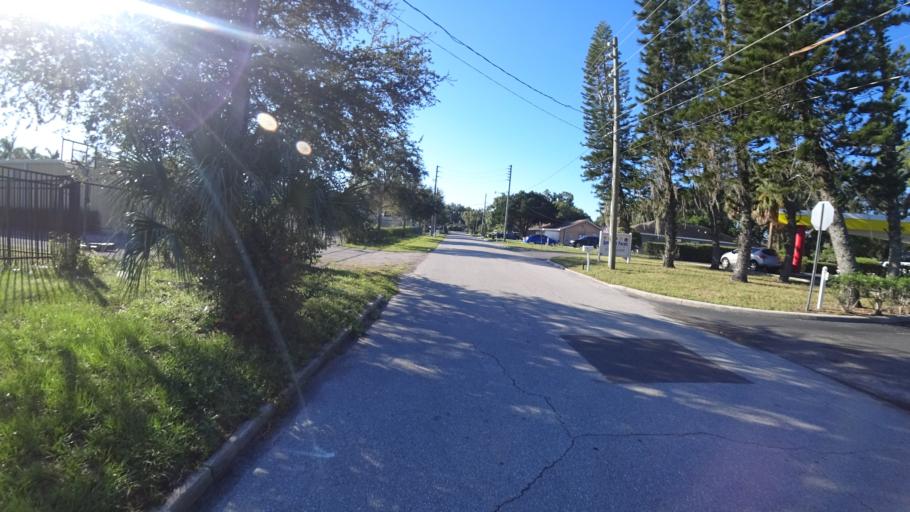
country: US
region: Florida
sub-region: Manatee County
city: Bradenton
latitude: 27.4835
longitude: -82.5726
